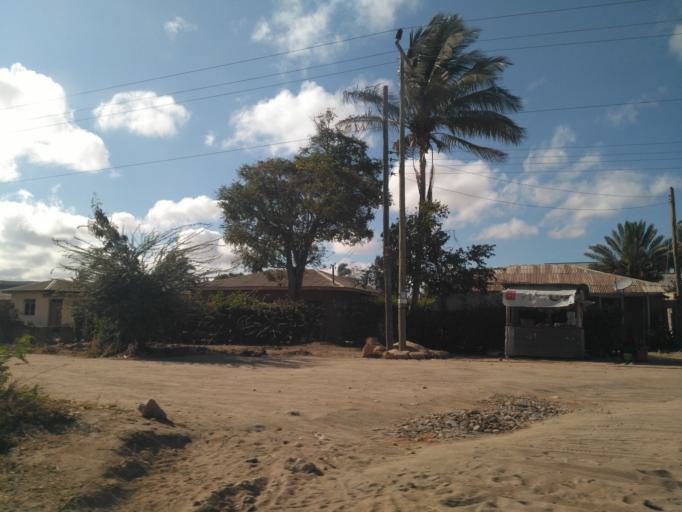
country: TZ
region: Dodoma
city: Dodoma
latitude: -6.1856
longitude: 35.7386
